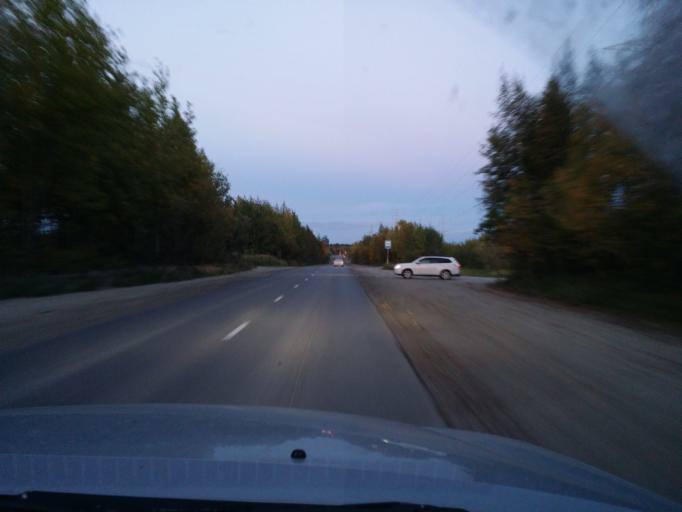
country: RU
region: Khanty-Mansiyskiy Avtonomnyy Okrug
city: Nizhnevartovsk
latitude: 60.9926
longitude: 76.4191
